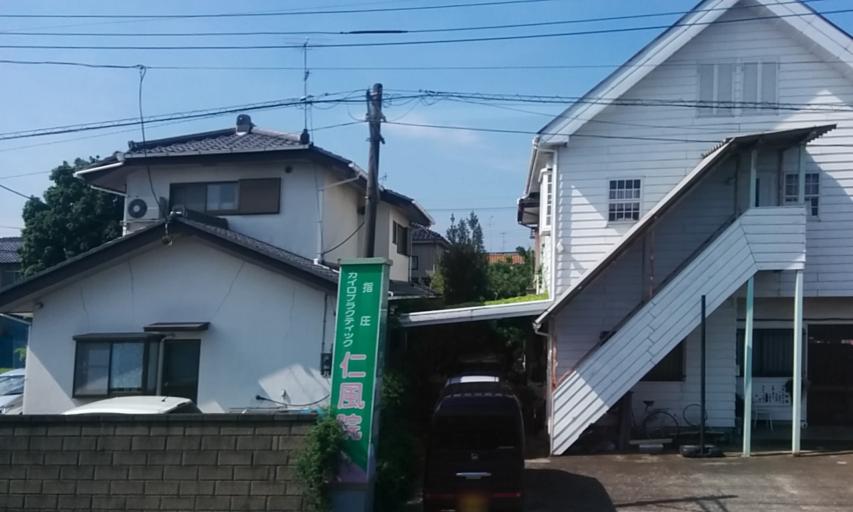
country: JP
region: Saitama
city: Kazo
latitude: 36.1170
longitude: 139.6122
